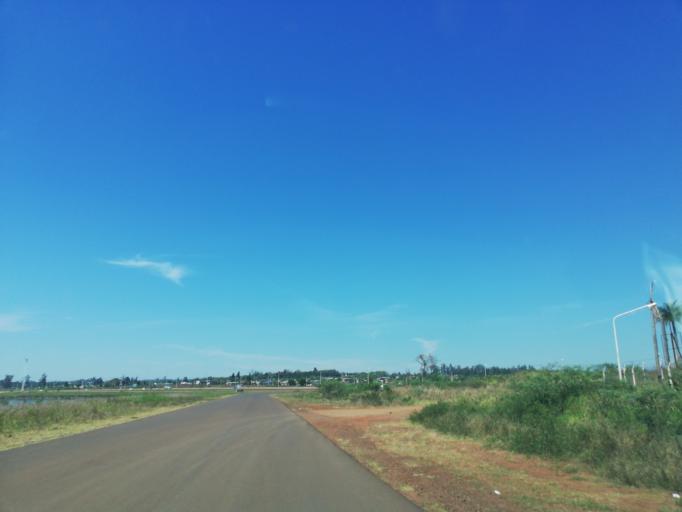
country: AR
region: Misiones
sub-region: Departamento de Capital
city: Posadas
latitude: -27.4260
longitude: -55.8697
